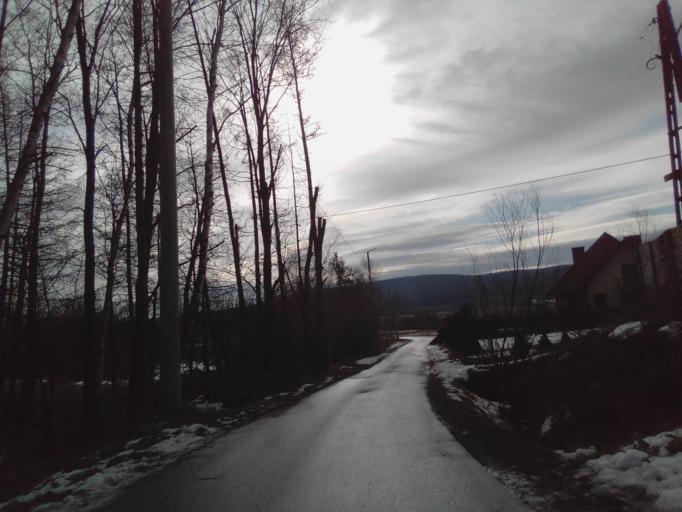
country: PL
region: Subcarpathian Voivodeship
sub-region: Powiat przemyski
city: Dubiecko
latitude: 49.8212
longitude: 22.4023
